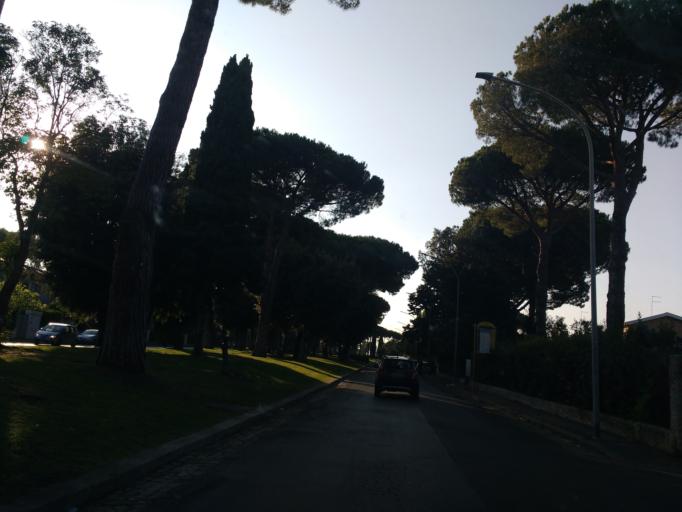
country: IT
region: Latium
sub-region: Citta metropolitana di Roma Capitale
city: Acilia-Castel Fusano-Ostia Antica
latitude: 41.7481
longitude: 12.3548
